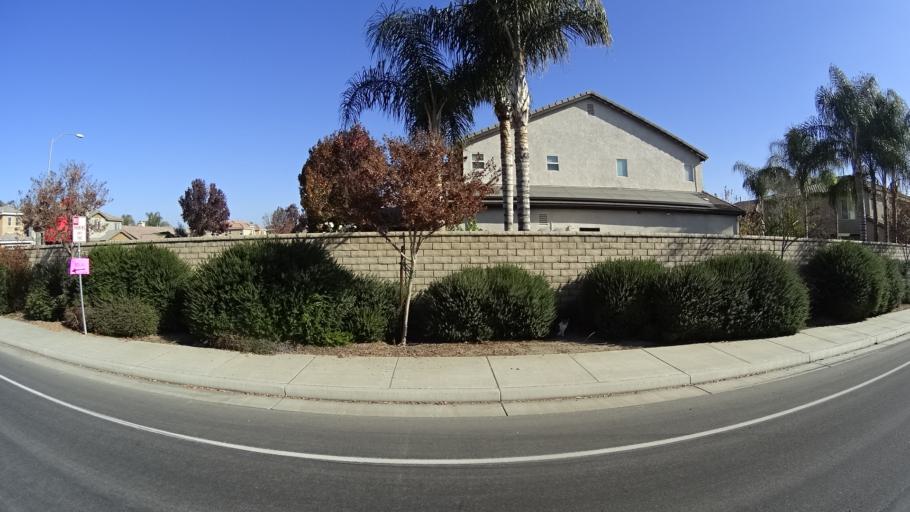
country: US
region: California
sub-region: Kern County
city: Greenacres
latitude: 35.3062
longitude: -119.1187
